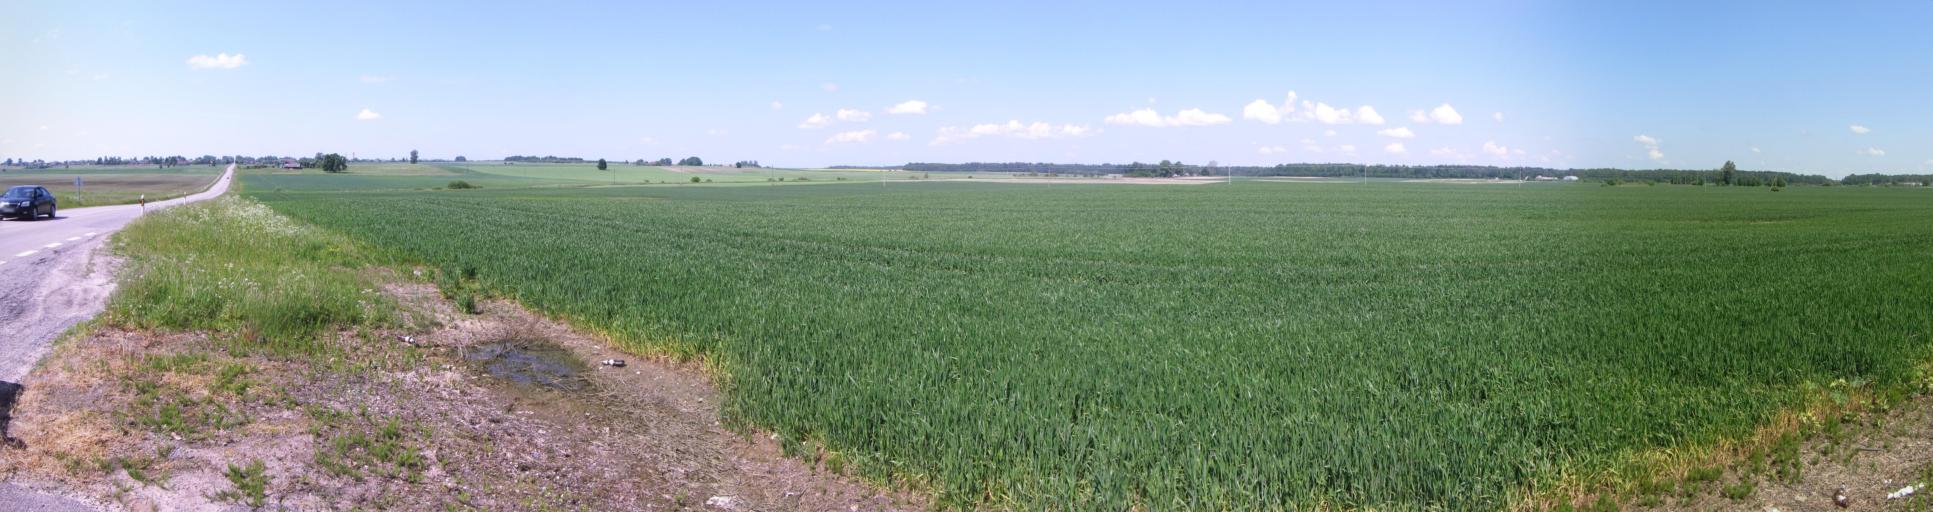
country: LT
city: Kaisiadorys
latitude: 54.8558
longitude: 24.3680
